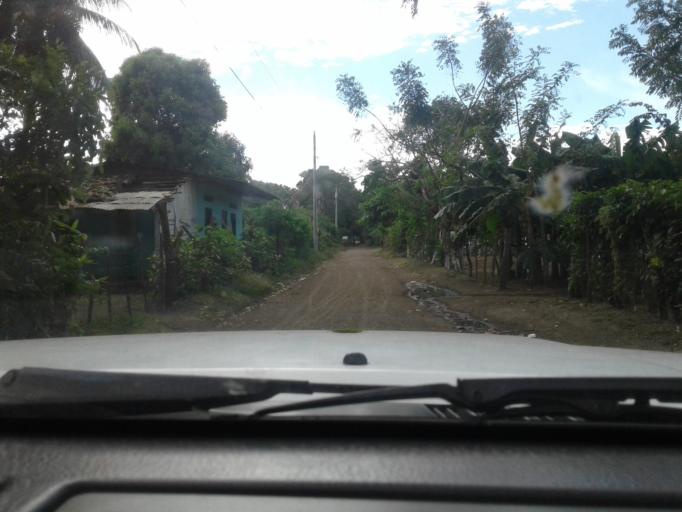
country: NI
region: Rivas
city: Potosi
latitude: 11.4814
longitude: -85.8383
